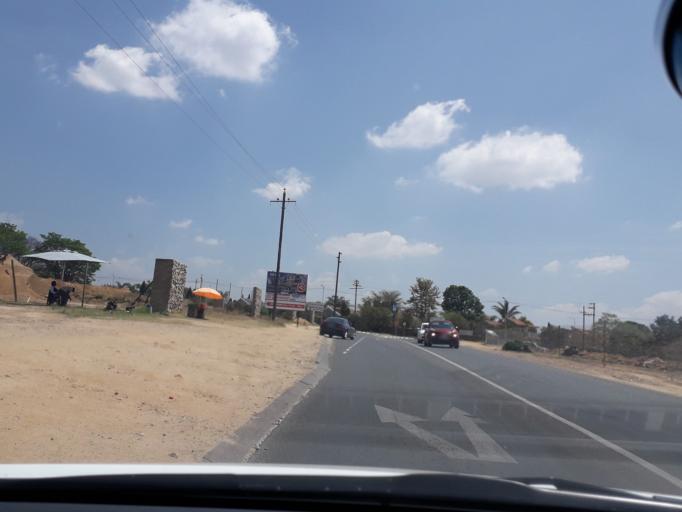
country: ZA
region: Gauteng
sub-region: City of Johannesburg Metropolitan Municipality
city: Midrand
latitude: -26.0091
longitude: 28.0787
